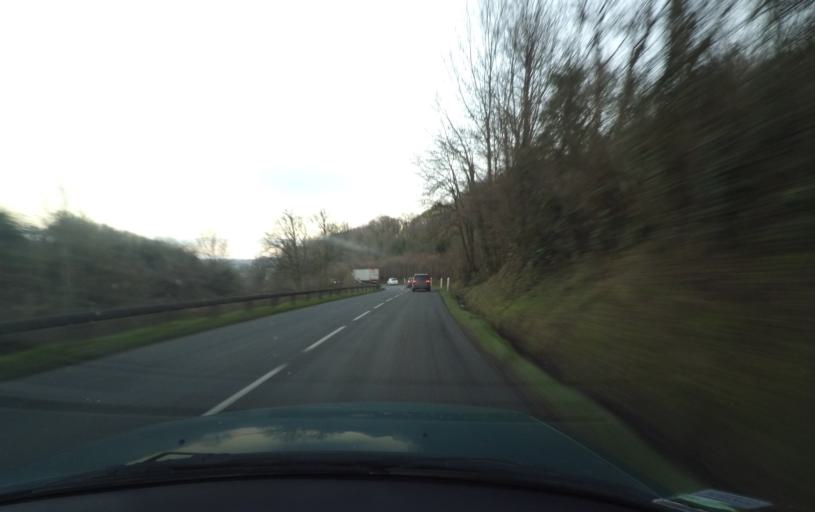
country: FR
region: Pays de la Loire
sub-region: Departement de la Mayenne
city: Bais
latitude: 48.2416
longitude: -0.3672
